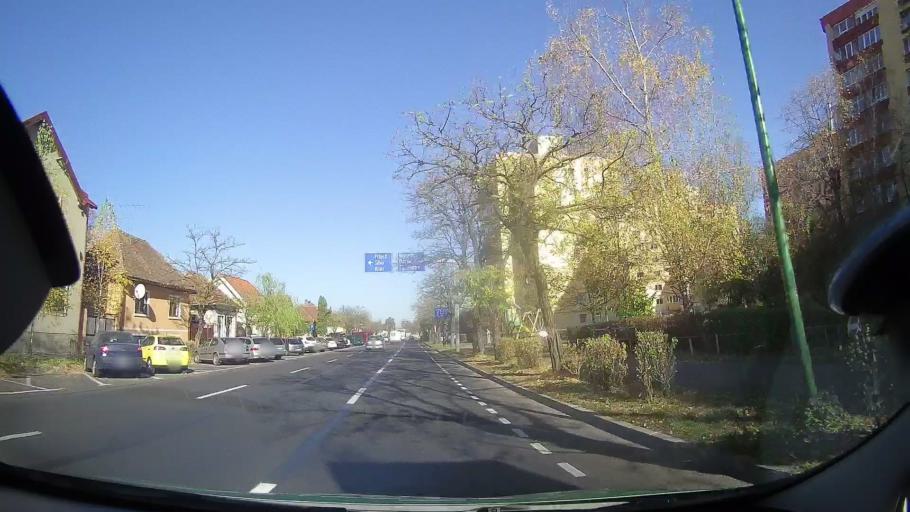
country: RO
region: Brasov
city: Brasov
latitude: 45.6625
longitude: 25.5816
